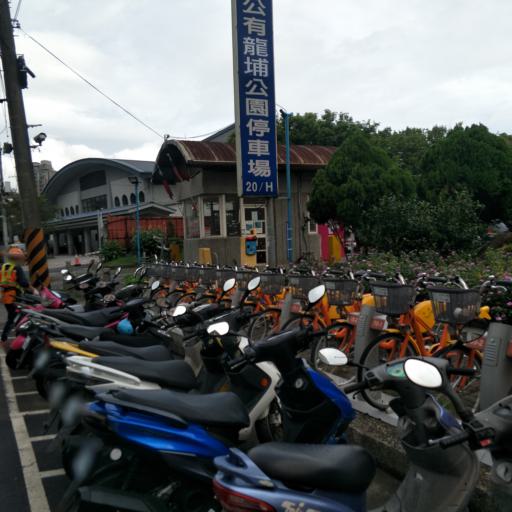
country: TW
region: Taiwan
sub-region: Taoyuan
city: Taoyuan
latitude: 24.9385
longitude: 121.3741
